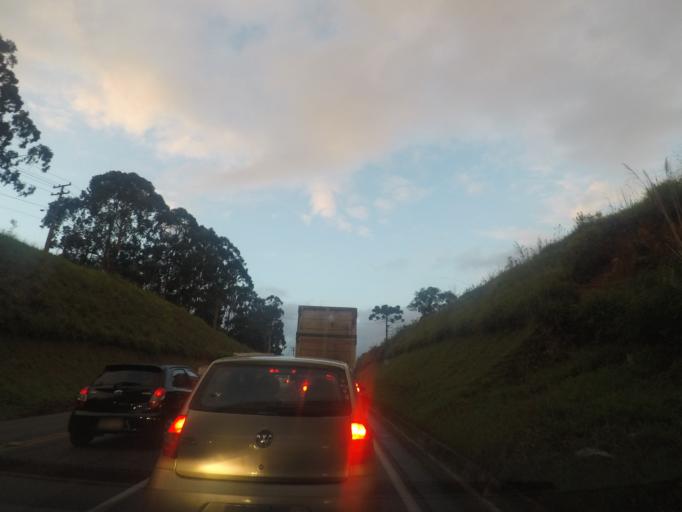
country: BR
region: Parana
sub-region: Curitiba
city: Curitiba
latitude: -25.4078
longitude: -49.3644
